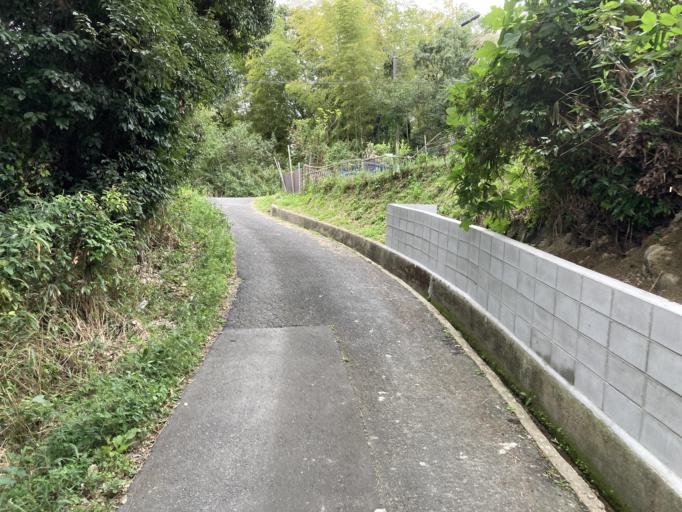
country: JP
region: Nara
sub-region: Ikoma-shi
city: Ikoma
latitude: 34.6784
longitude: 135.6997
